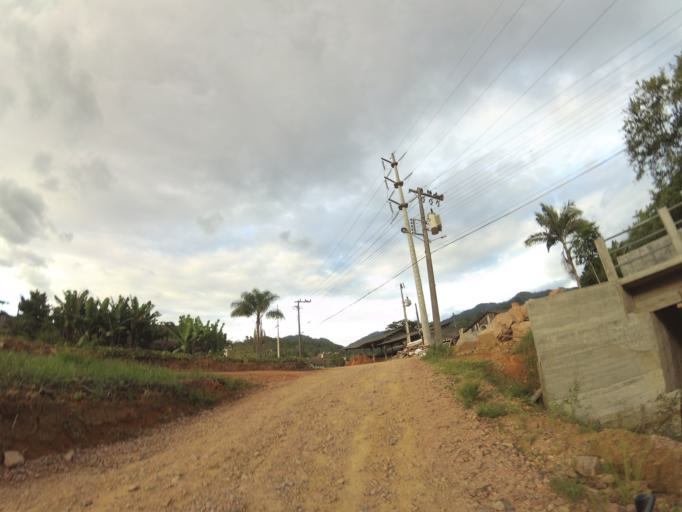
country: BR
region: Santa Catarina
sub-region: Pomerode
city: Pomerode
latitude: -26.7712
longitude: -49.1640
